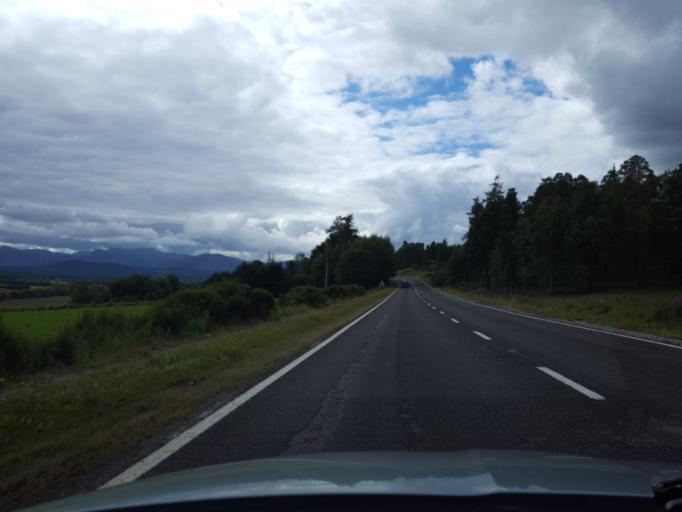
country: GB
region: Scotland
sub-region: Highland
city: Grantown on Spey
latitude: 57.2932
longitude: -3.6649
